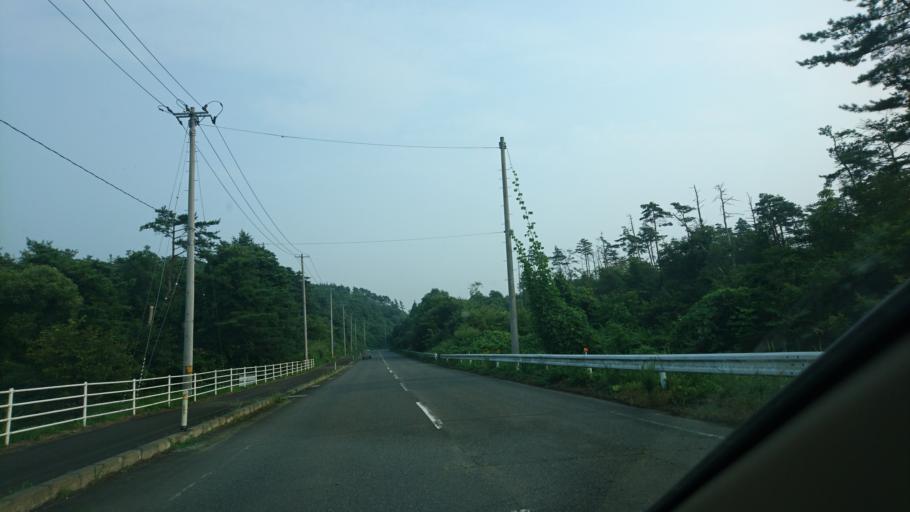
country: JP
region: Iwate
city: Kitakami
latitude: 39.2249
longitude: 141.1909
